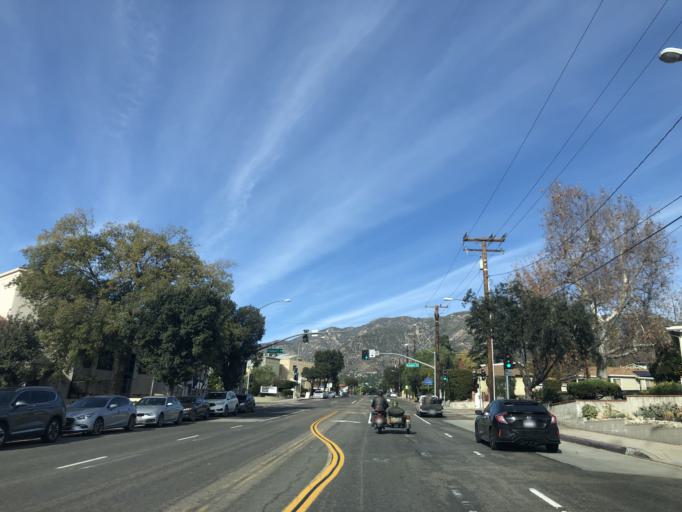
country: US
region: California
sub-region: Los Angeles County
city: La Crescenta-Montrose
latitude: 34.2207
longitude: -118.2399
